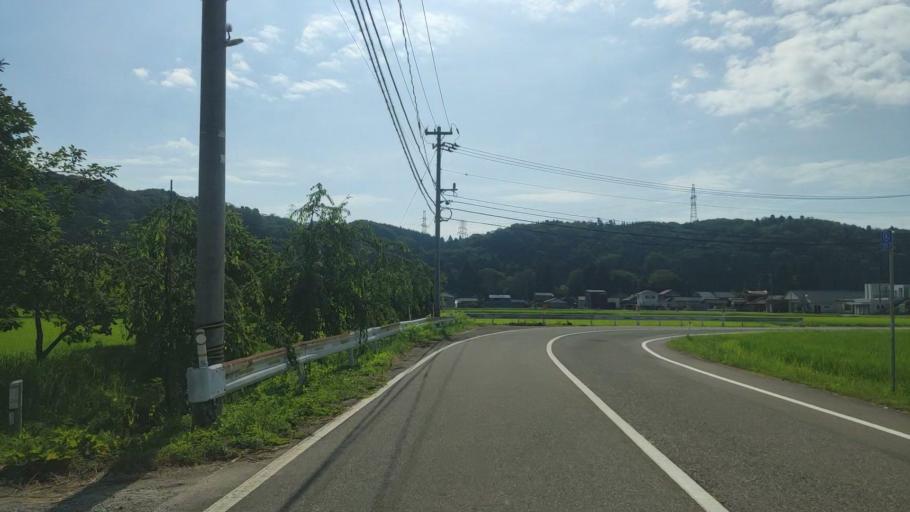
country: JP
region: Ishikawa
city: Komatsu
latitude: 36.3733
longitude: 136.4975
